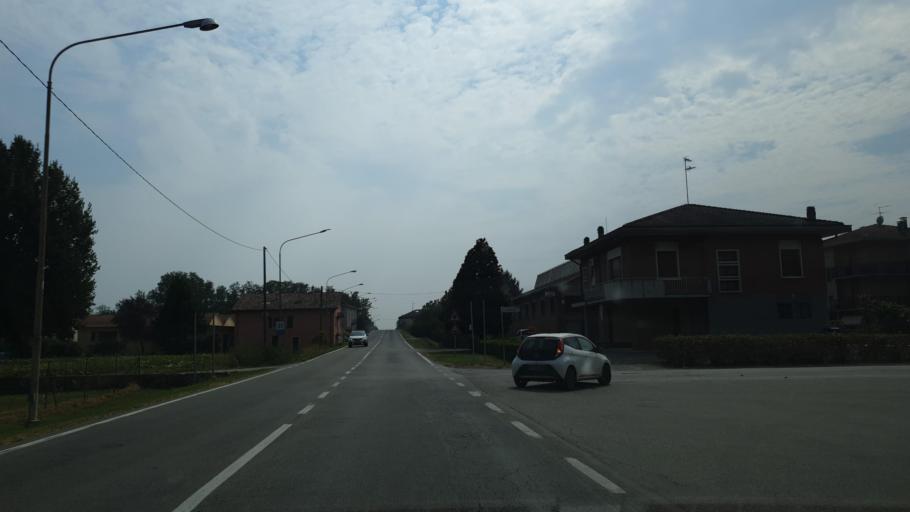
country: IT
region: Emilia-Romagna
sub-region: Provincia di Parma
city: Roccabianca
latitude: 44.9682
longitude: 10.2139
